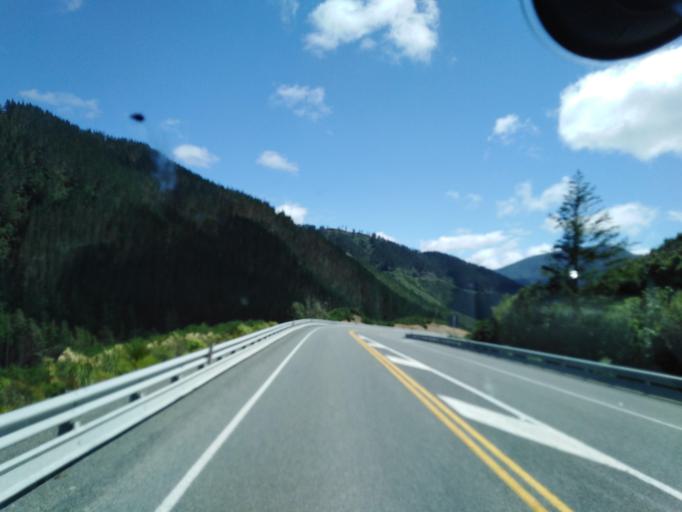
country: NZ
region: Nelson
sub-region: Nelson City
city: Nelson
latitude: -41.1896
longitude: 173.5540
